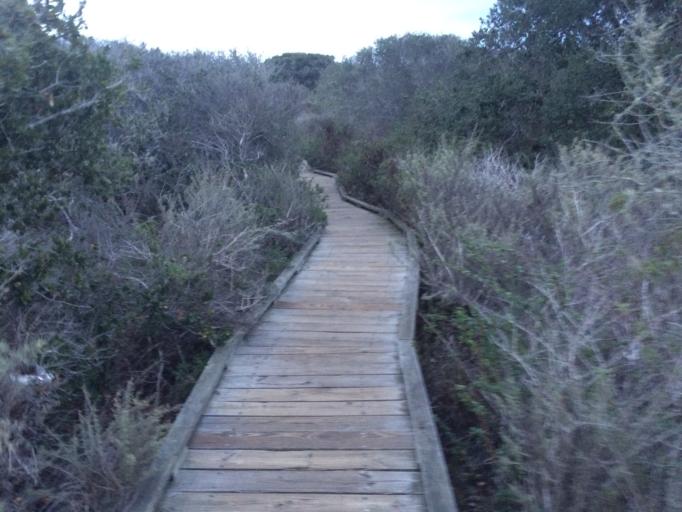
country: US
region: California
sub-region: San Luis Obispo County
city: Los Osos
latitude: 35.3340
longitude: -120.8290
